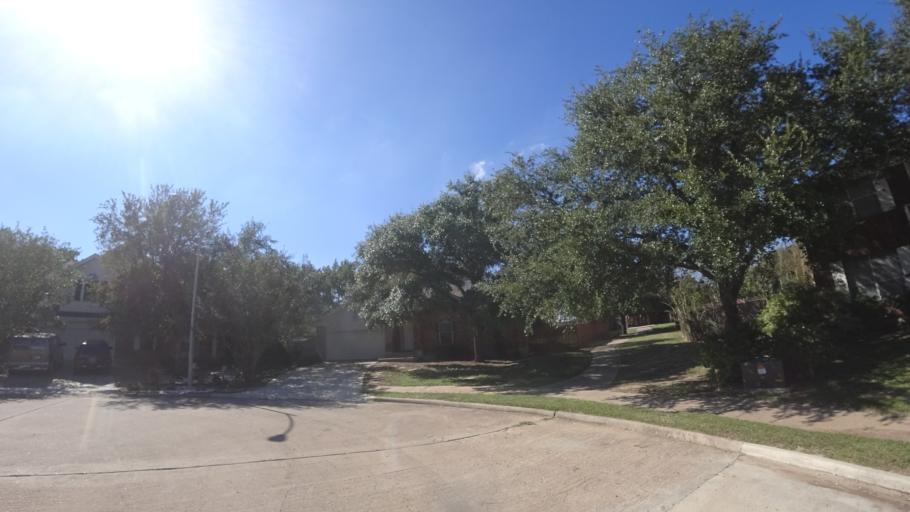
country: US
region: Texas
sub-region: Travis County
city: Manor
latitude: 30.3524
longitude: -97.6150
